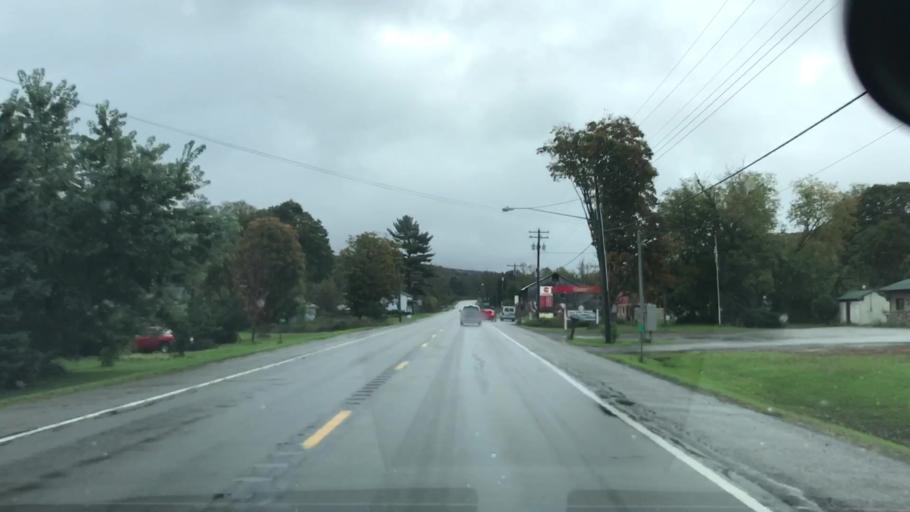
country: US
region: New York
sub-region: Erie County
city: Springville
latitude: 42.4024
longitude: -78.6841
